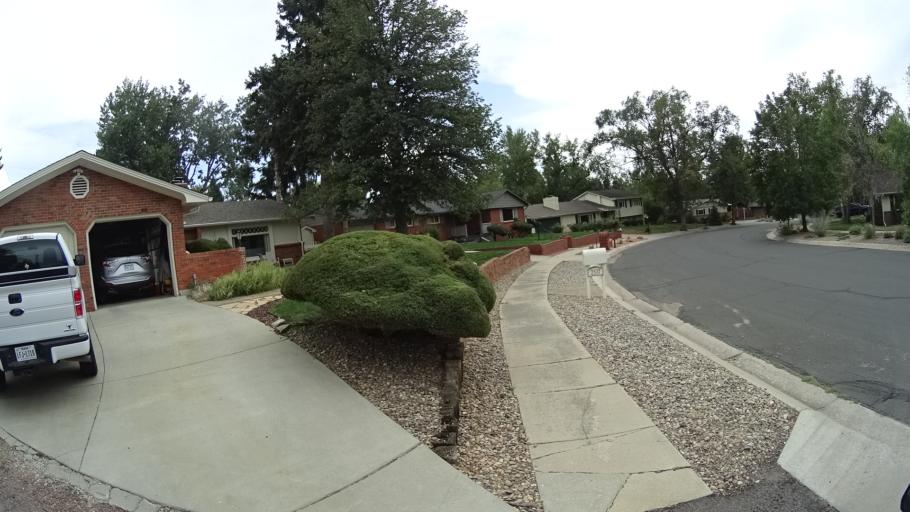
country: US
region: Colorado
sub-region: El Paso County
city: Colorado Springs
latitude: 38.8698
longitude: -104.7802
